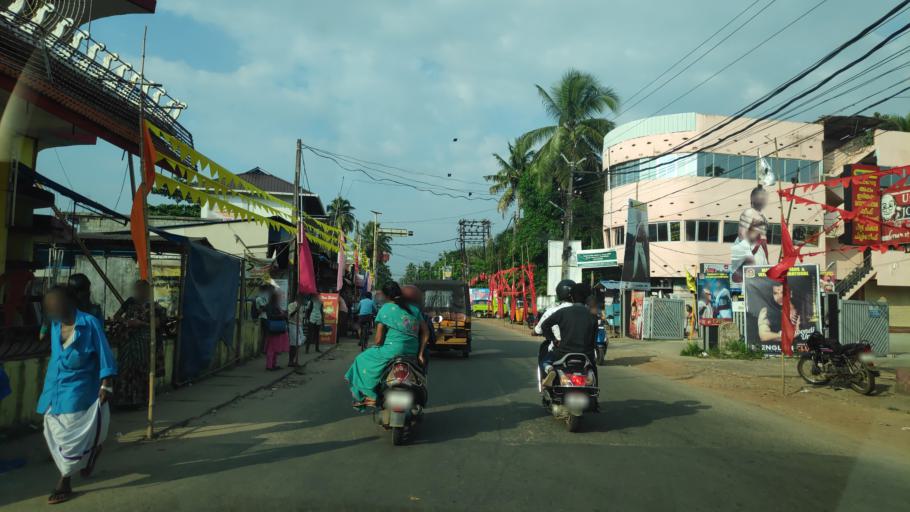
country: IN
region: Kerala
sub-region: Alappuzha
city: Alleppey
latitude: 9.5165
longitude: 76.3384
